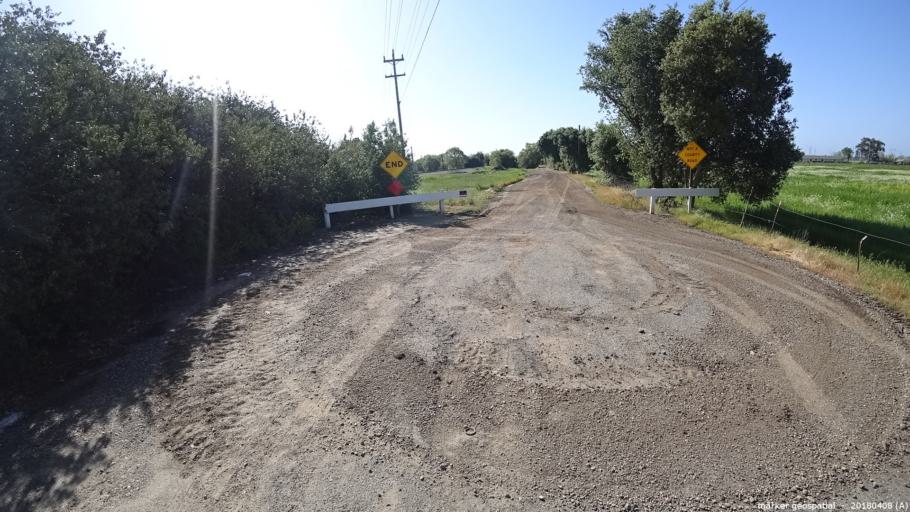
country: US
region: California
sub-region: Sacramento County
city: Elk Grove
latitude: 38.3614
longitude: -121.3472
